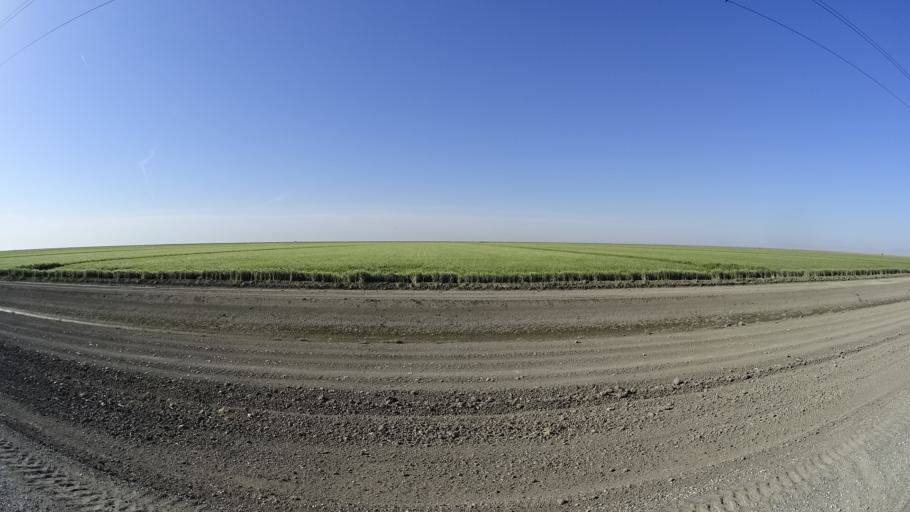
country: US
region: California
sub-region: Kings County
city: Corcoran
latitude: 36.0797
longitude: -119.6590
